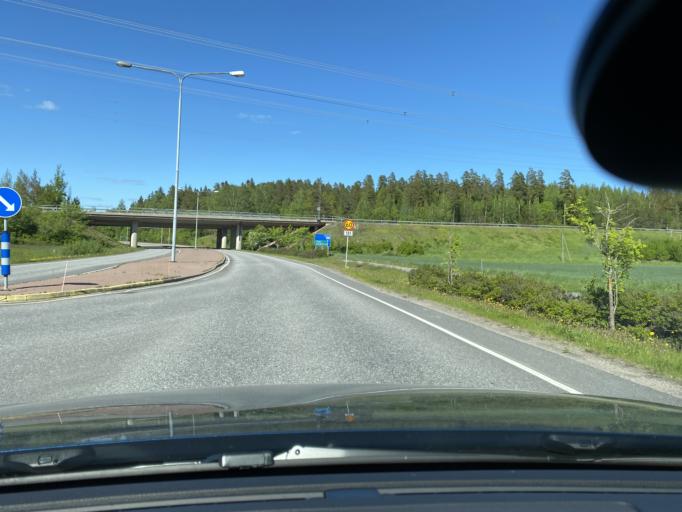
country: FI
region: Varsinais-Suomi
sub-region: Turku
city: Paimio
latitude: 60.4240
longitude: 22.6705
